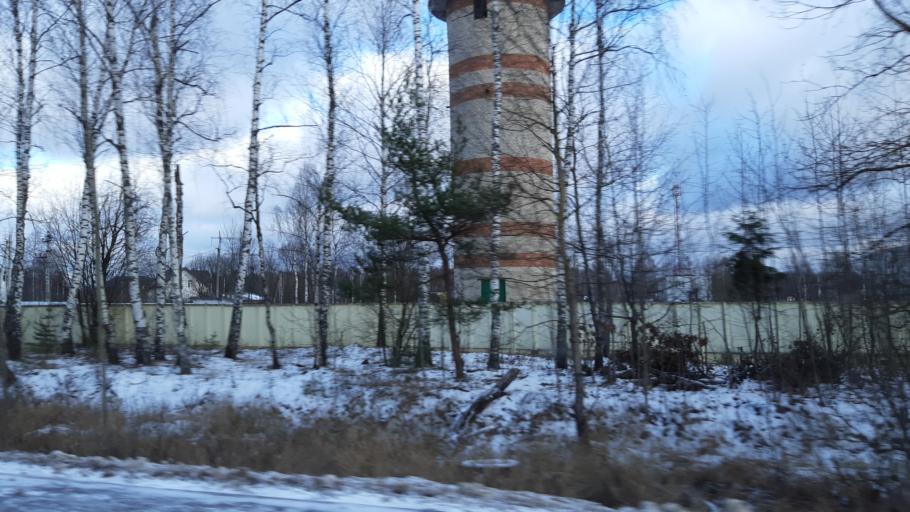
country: RU
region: Moskovskaya
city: Noginsk-9
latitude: 55.9529
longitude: 38.5504
